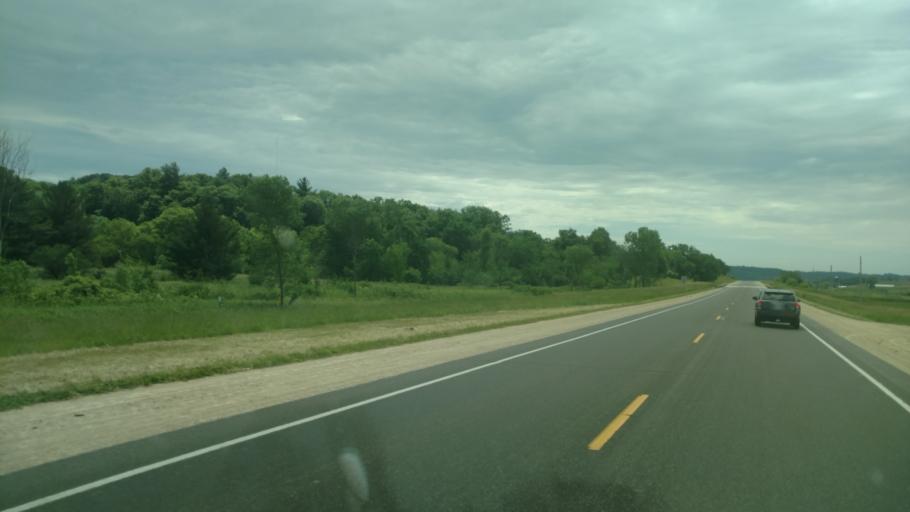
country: US
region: Wisconsin
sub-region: Monroe County
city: Tomah
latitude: 43.8658
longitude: -90.4739
